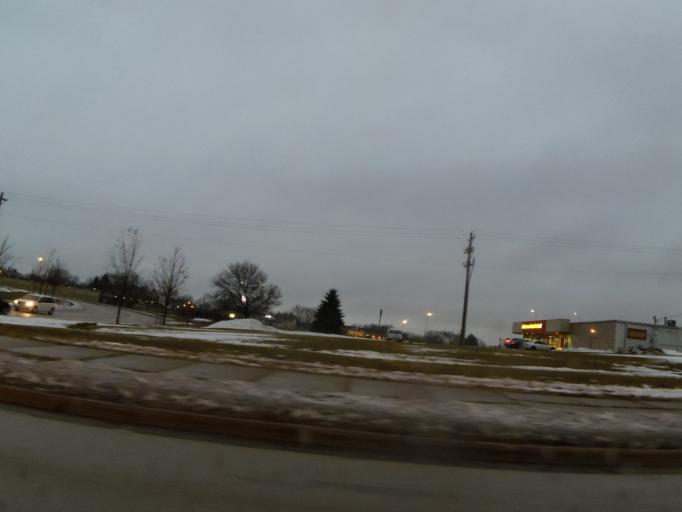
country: US
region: Minnesota
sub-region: Olmsted County
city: Rochester
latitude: 44.0415
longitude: -92.4856
